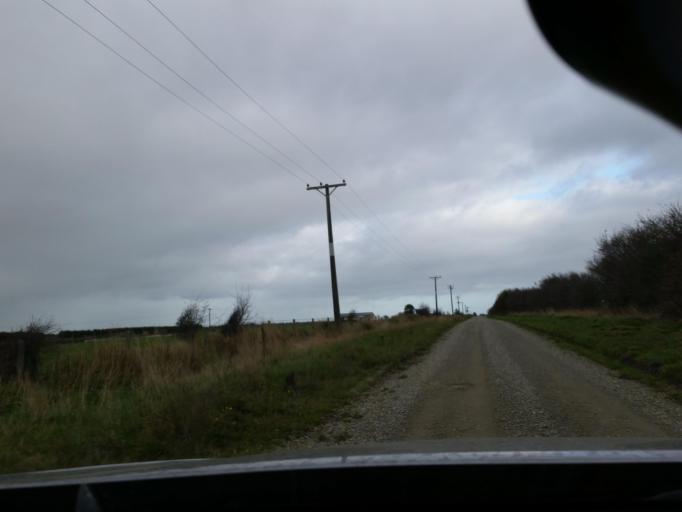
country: NZ
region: Southland
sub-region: Southland District
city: Winton
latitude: -46.2233
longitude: 168.3672
